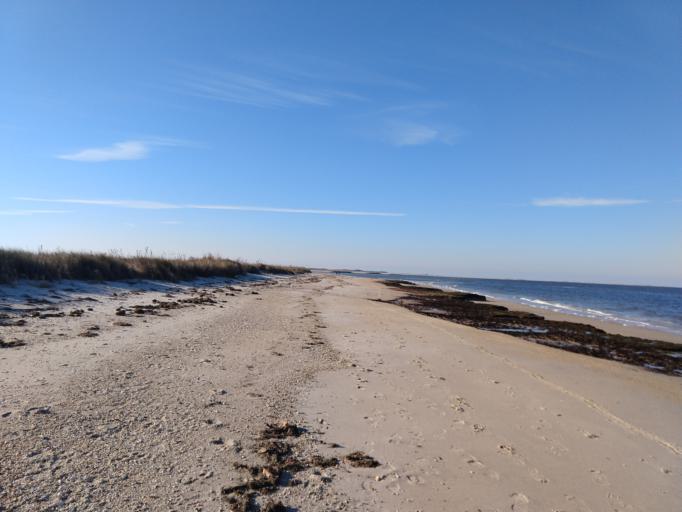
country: US
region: Virginia
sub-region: City of Poquoson
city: Poquoson
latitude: 37.1015
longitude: -76.2811
